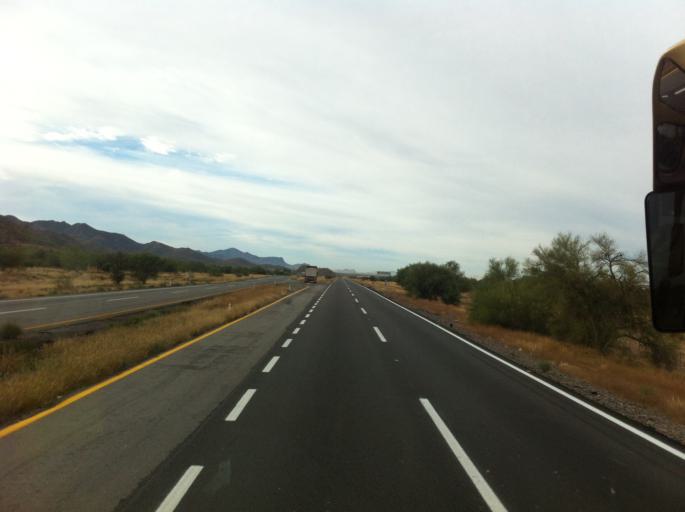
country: MX
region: Sonora
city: Hermosillo
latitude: 28.6533
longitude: -111.0048
